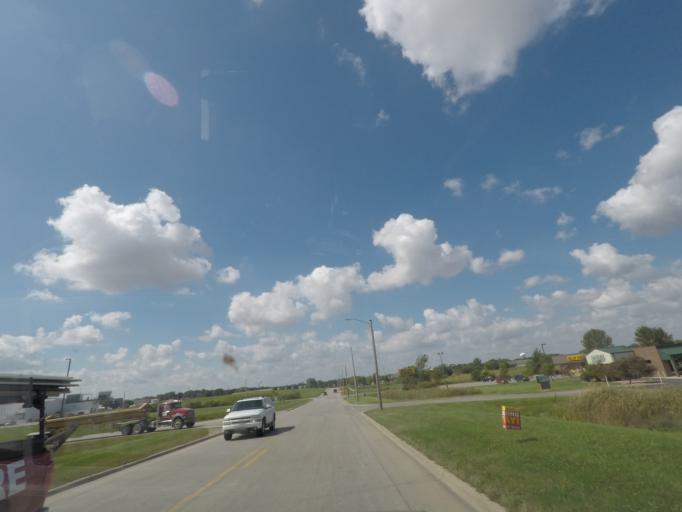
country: US
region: Iowa
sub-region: Story County
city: Nevada
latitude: 42.0098
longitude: -93.4357
